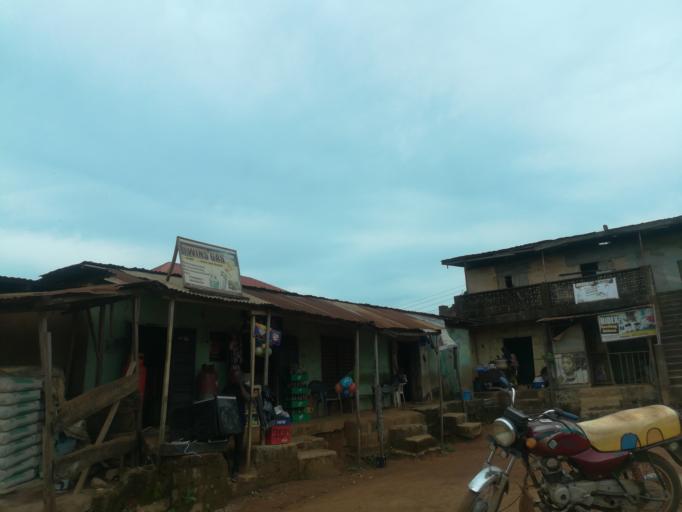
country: NG
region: Oyo
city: Ibadan
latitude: 7.3760
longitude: 3.9573
